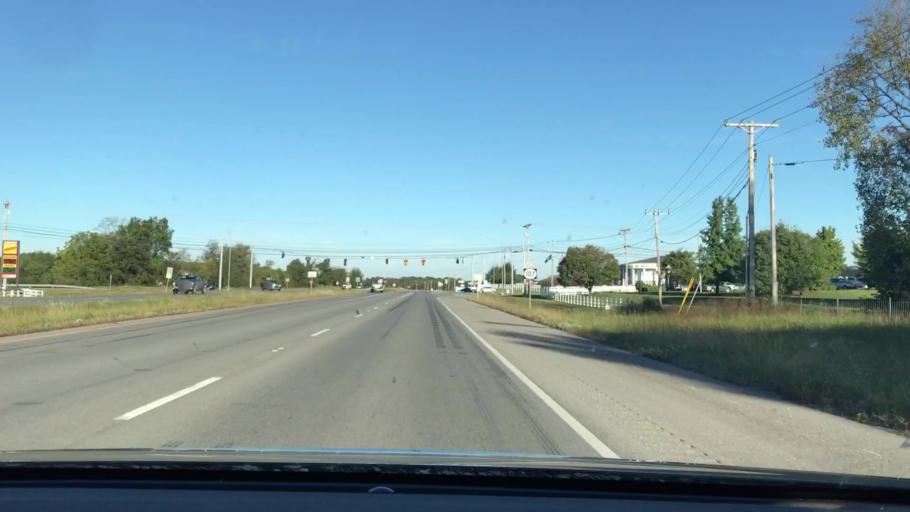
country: US
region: Kentucky
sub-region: Christian County
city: Hopkinsville
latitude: 36.8208
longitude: -87.5032
